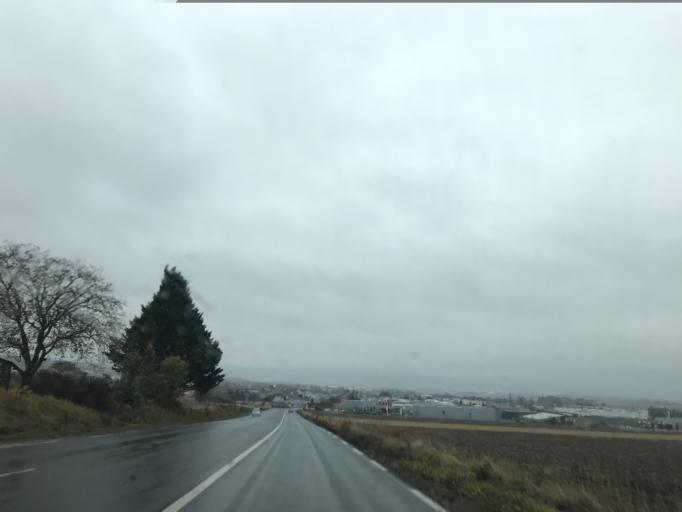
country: FR
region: Auvergne
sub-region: Departement du Puy-de-Dome
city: Dallet
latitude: 45.7728
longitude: 3.2172
